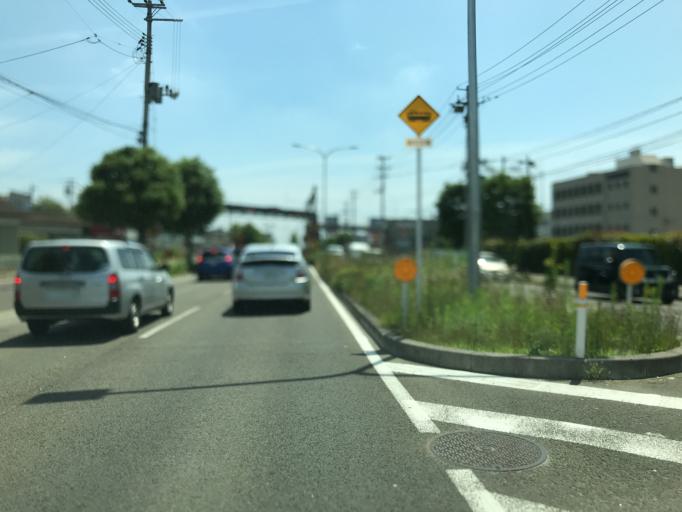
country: JP
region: Miyagi
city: Sendai-shi
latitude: 38.2730
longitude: 140.8955
